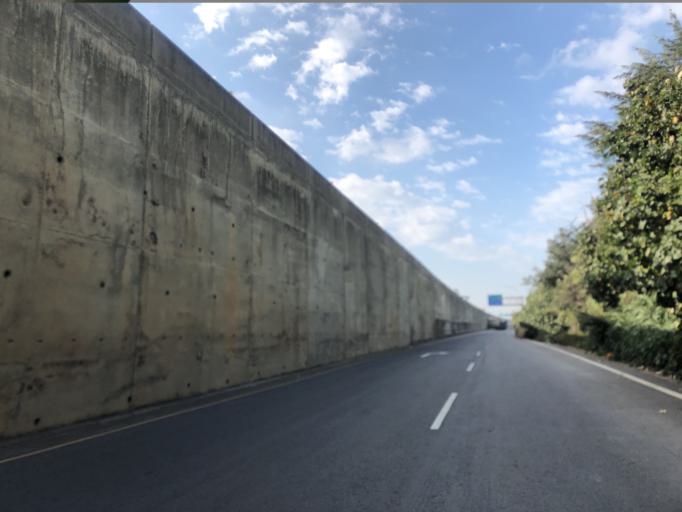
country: TW
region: Taiwan
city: Taoyuan City
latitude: 25.0649
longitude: 121.1108
